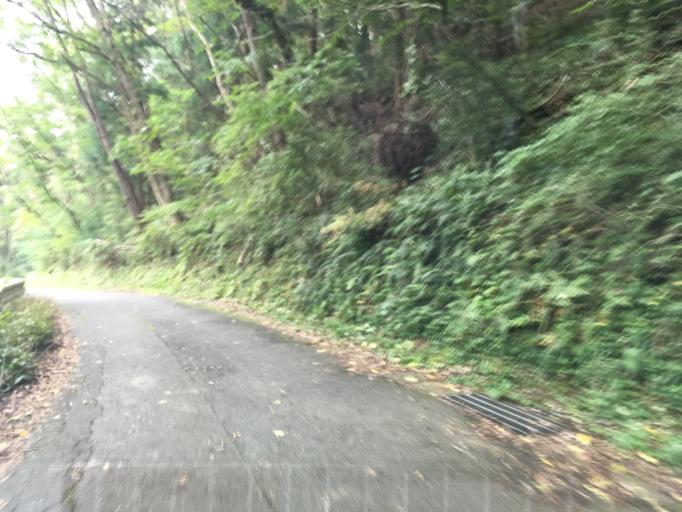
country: JP
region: Fukushima
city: Fukushima-shi
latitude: 37.7764
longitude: 140.4763
